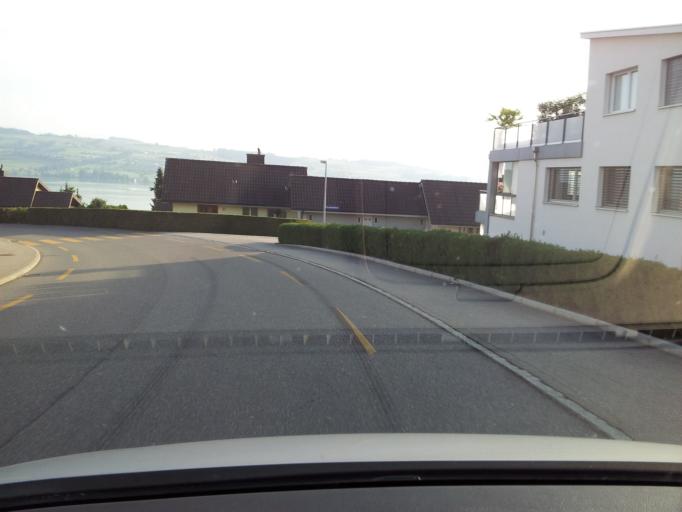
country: CH
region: Lucerne
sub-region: Sursee District
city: Eich
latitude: 47.1551
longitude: 8.1646
